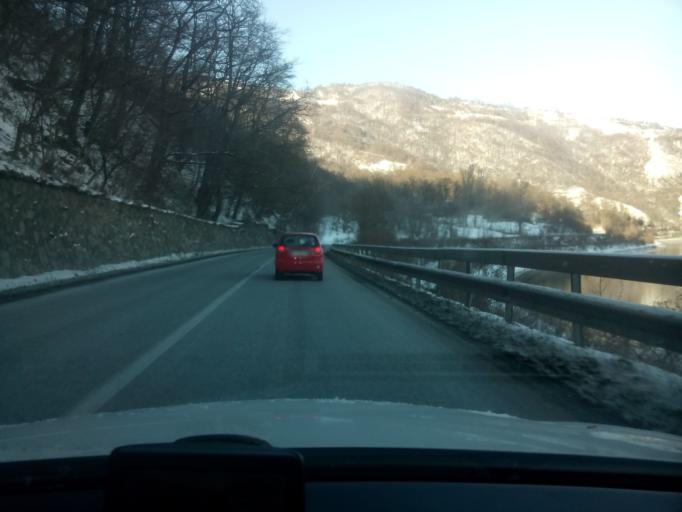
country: RO
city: Cainenii Mici
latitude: 45.4763
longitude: 24.2918
